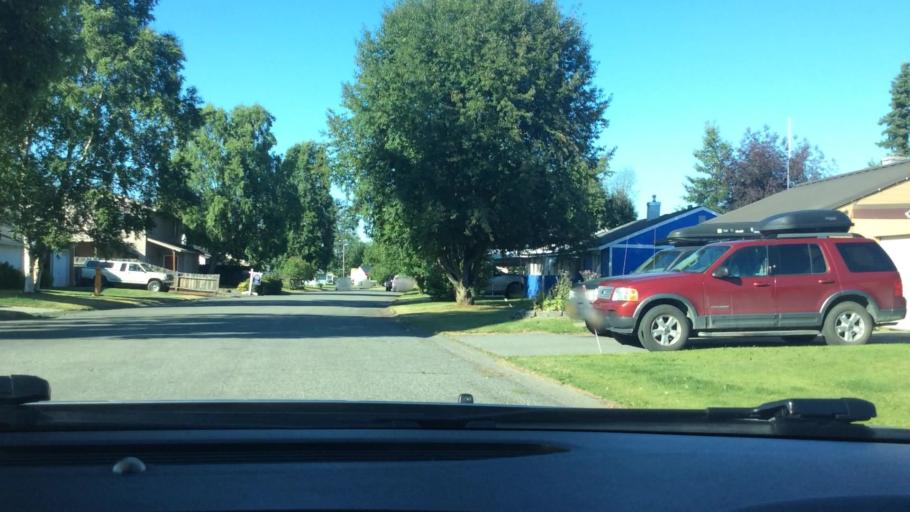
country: US
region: Alaska
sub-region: Anchorage Municipality
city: Anchorage
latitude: 61.2065
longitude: -149.7672
